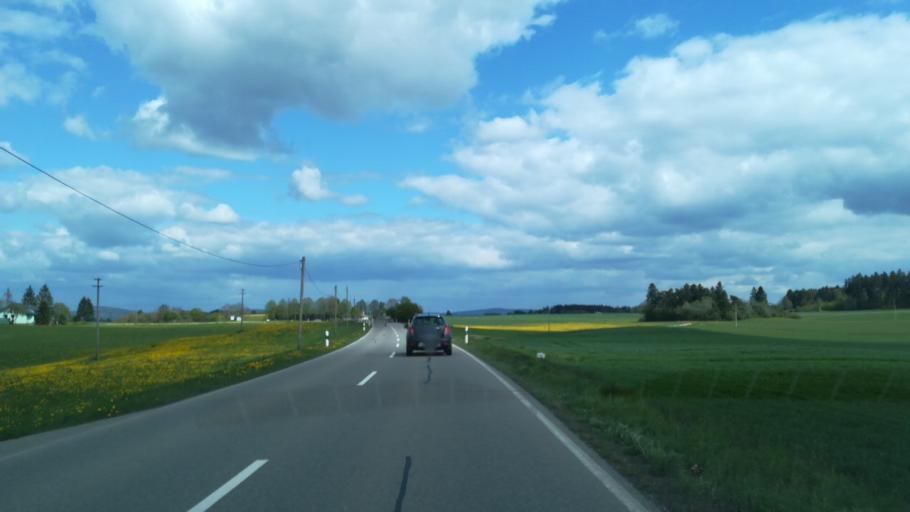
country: DE
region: Baden-Wuerttemberg
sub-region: Freiburg Region
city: Bonndorf im Schwarzwald
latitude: 47.8206
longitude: 8.3660
